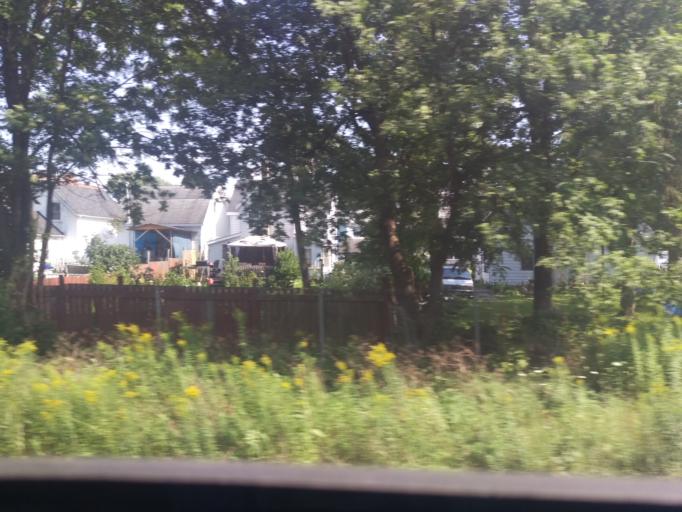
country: CA
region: Ontario
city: Brockville
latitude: 44.5968
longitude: -75.6847
